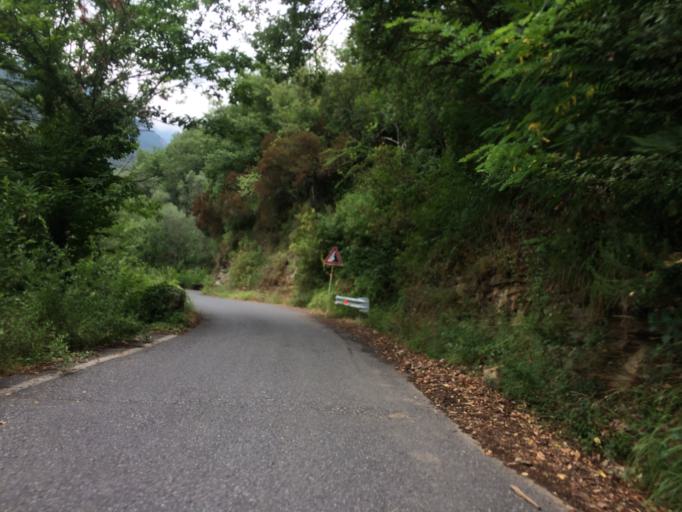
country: IT
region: Liguria
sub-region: Provincia di Imperia
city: Castel Vittorio
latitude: 43.9394
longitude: 7.6862
